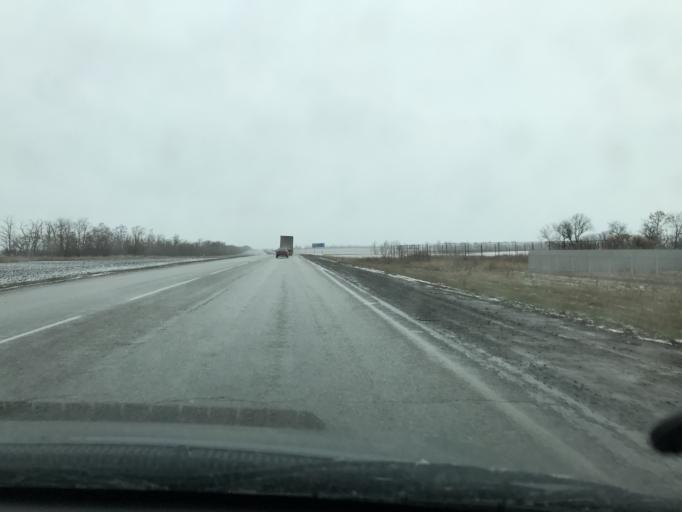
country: RU
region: Rostov
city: Kagal'nitskaya
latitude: 46.8729
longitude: 40.1640
